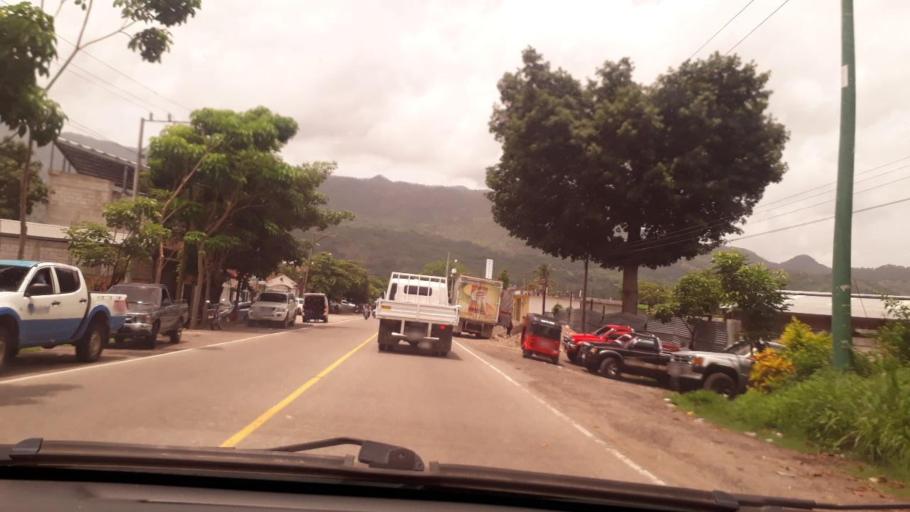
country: GT
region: Chiquimula
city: Quezaltepeque
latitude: 14.6333
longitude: -89.4443
